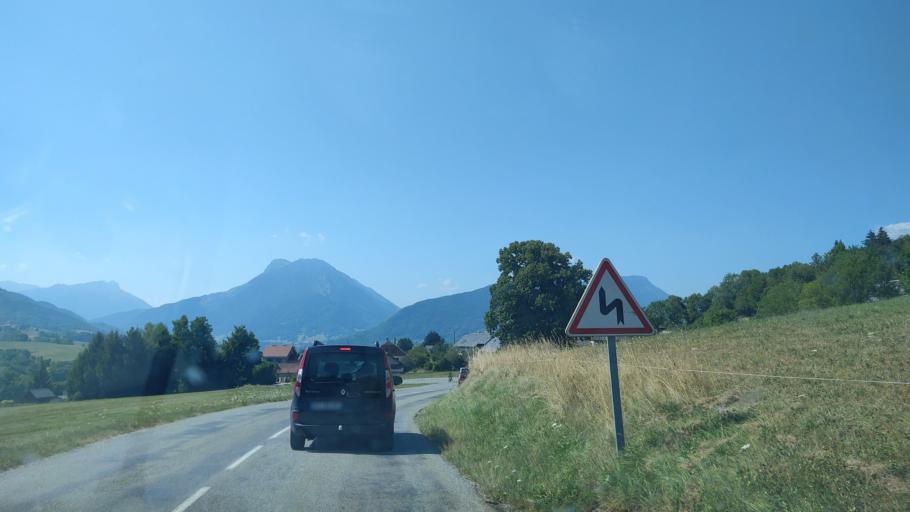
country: FR
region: Rhone-Alpes
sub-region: Departement de la Haute-Savoie
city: Gruffy
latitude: 45.7473
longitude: 6.1144
